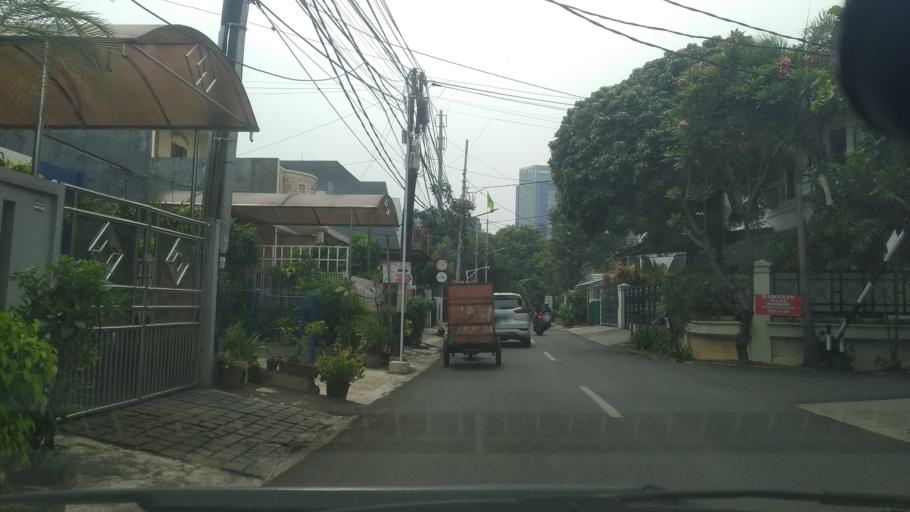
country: ID
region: Banten
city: South Tangerang
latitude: -6.2631
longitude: 106.7772
